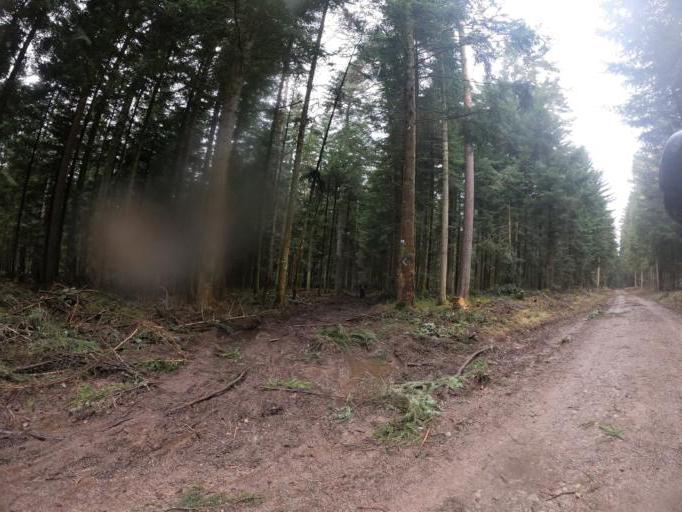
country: DE
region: Baden-Wuerttemberg
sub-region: Karlsruhe Region
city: Neuweiler
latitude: 48.6998
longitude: 8.6108
